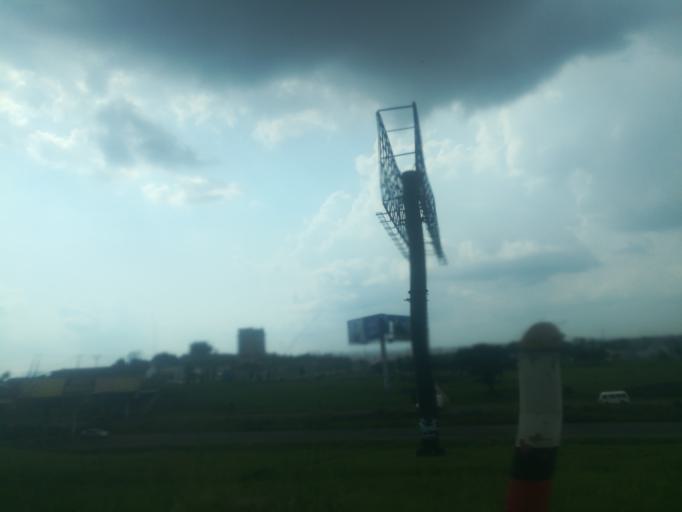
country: NG
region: Oyo
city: Ibadan
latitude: 7.3304
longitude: 3.8762
